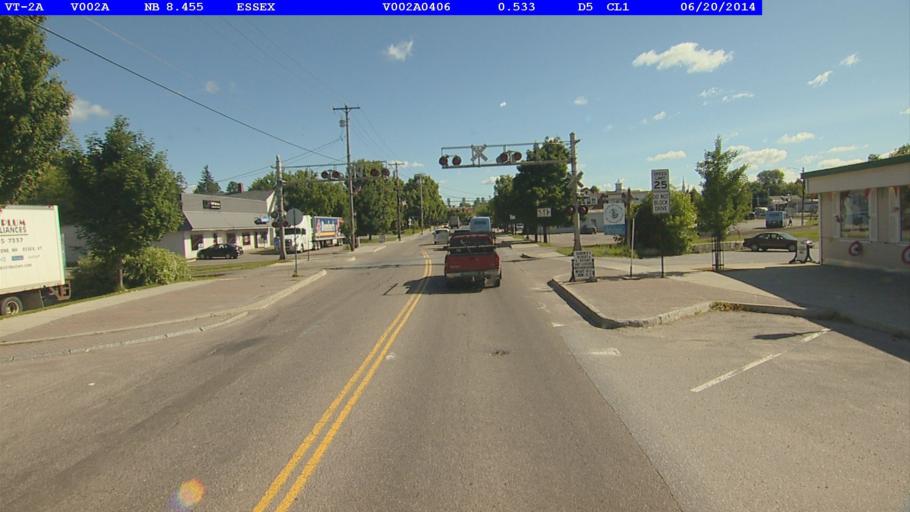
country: US
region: Vermont
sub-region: Chittenden County
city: Essex Junction
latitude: 44.4887
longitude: -73.1123
